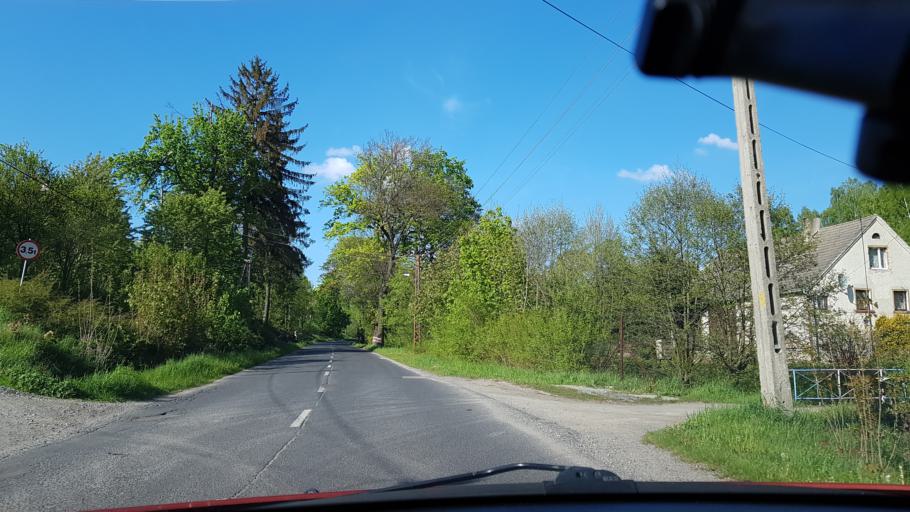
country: PL
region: Lower Silesian Voivodeship
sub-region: Powiat klodzki
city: Nowa Ruda
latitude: 50.5870
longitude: 16.5372
